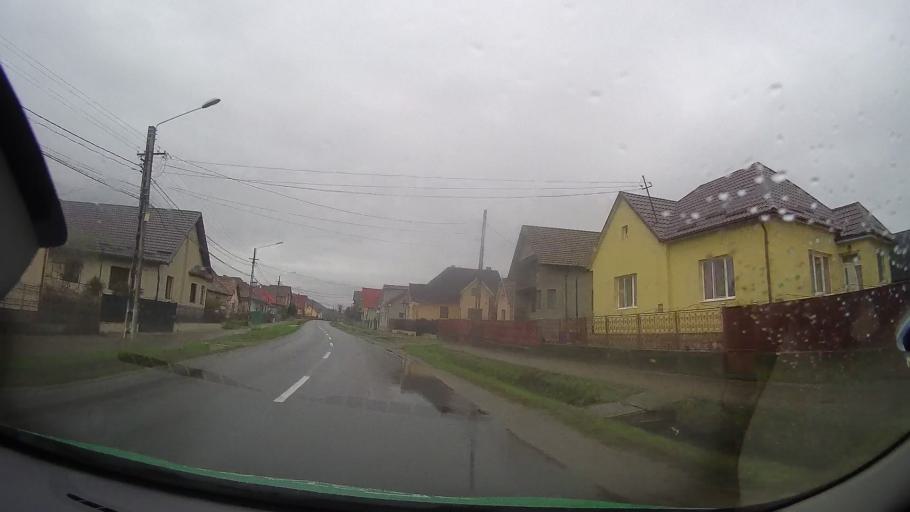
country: RO
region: Bistrita-Nasaud
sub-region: Municipiul Bistrita
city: Viisoara
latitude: 47.0742
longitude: 24.4355
